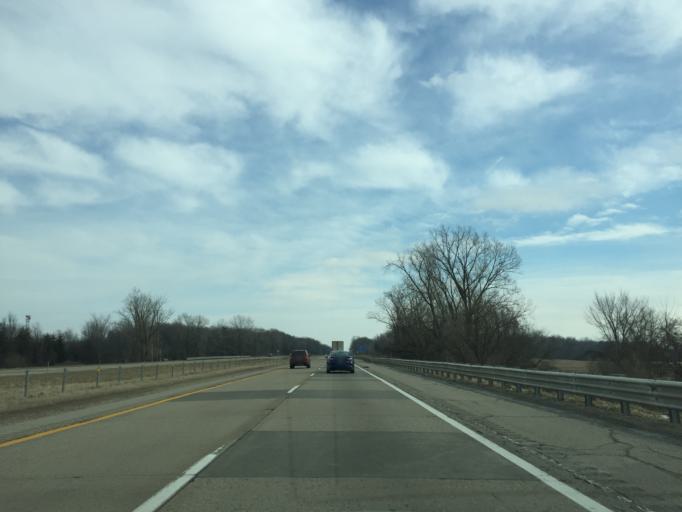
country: US
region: Michigan
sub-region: Ionia County
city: Saranac
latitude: 42.8792
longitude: -85.1708
